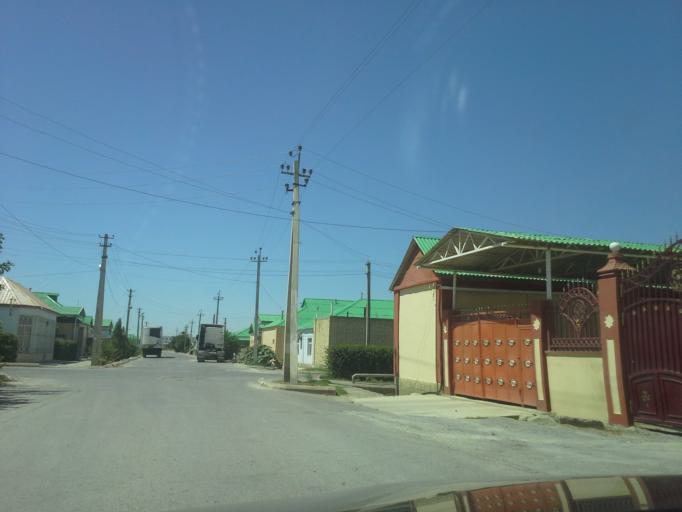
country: TM
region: Ahal
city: Abadan
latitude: 38.0445
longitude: 58.2241
